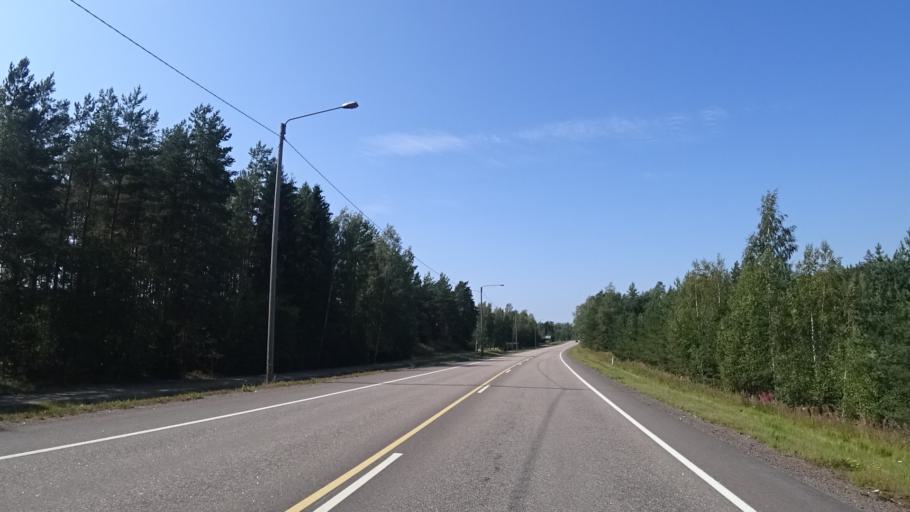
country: FI
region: Kymenlaakso
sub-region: Kotka-Hamina
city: Karhula
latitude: 60.5629
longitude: 27.0580
